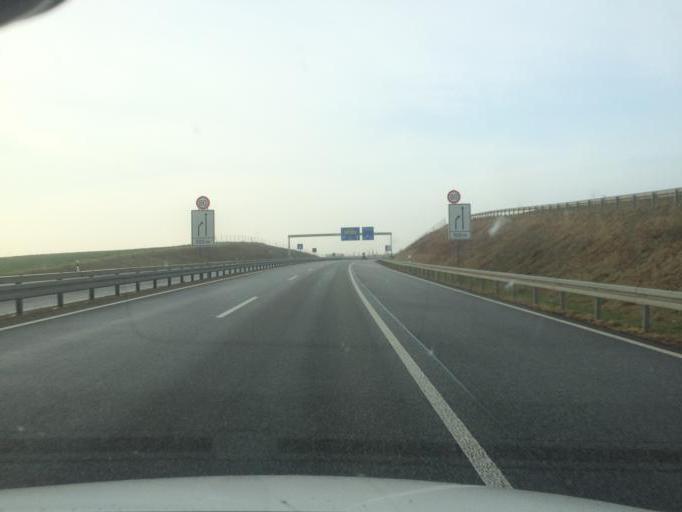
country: DE
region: Thuringia
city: Nohra
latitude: 51.4944
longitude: 10.7173
